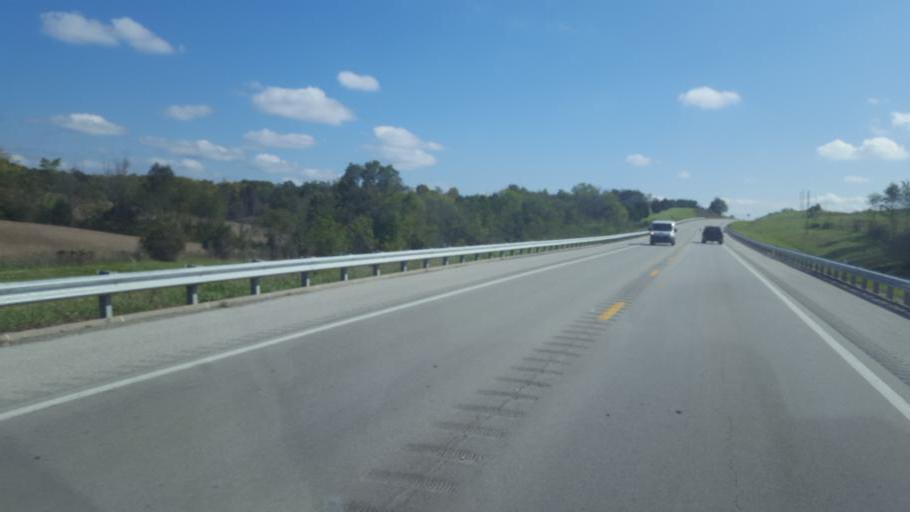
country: US
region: Kentucky
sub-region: Mason County
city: Maysville
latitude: 38.5787
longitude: -83.6643
